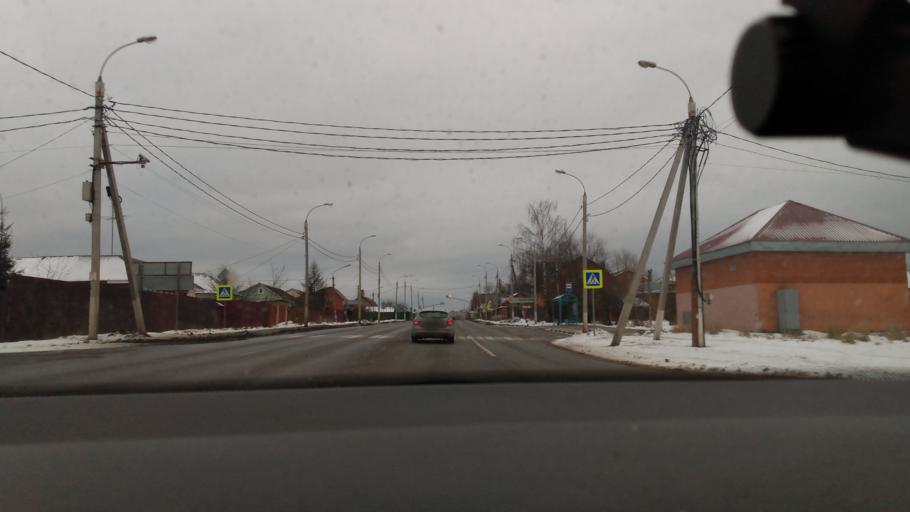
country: RU
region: Moskovskaya
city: Yegor'yevsk
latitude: 55.3782
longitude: 39.0684
